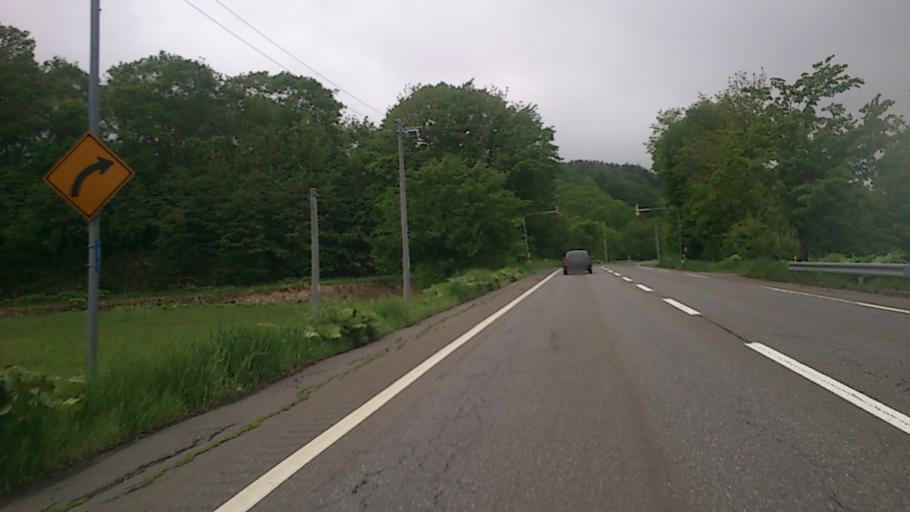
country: JP
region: Hokkaido
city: Obihiro
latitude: 42.8311
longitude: 143.7383
